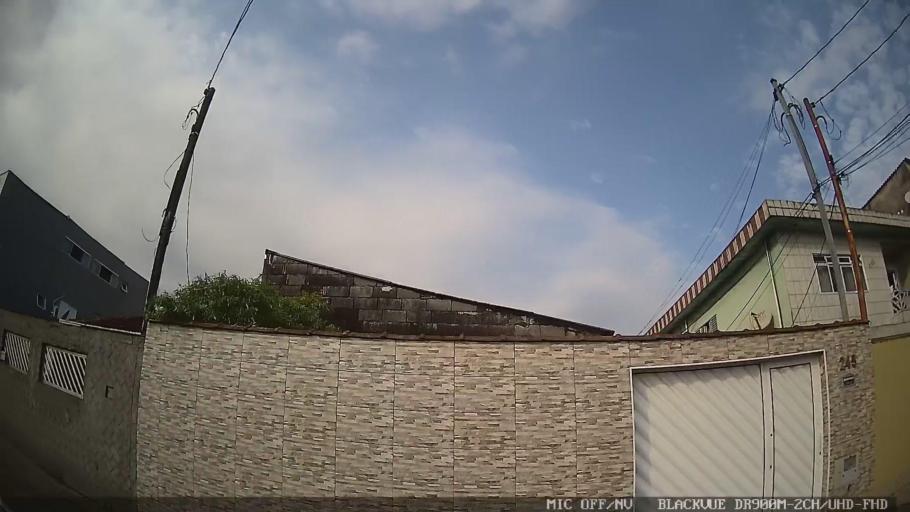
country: BR
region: Sao Paulo
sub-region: Guaruja
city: Guaruja
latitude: -23.9533
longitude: -46.2829
